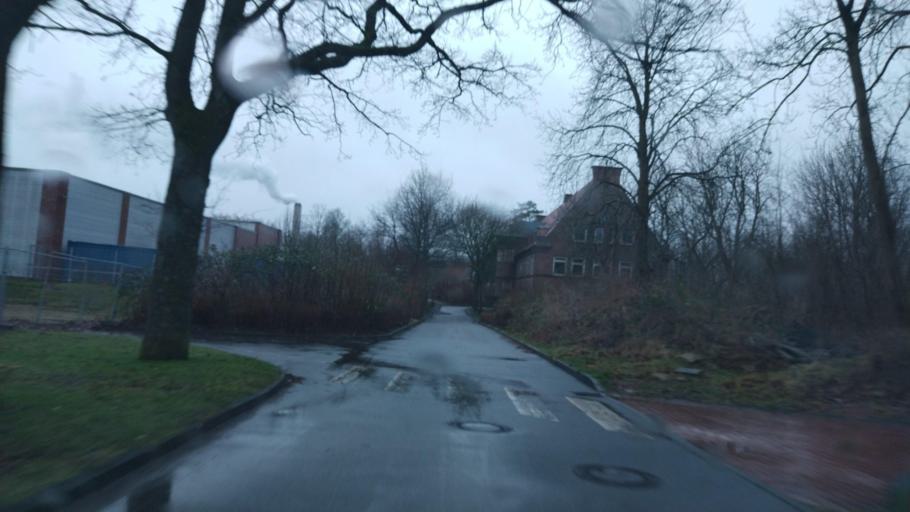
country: DE
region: Schleswig-Holstein
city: Schleswig
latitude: 54.5207
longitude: 9.5493
